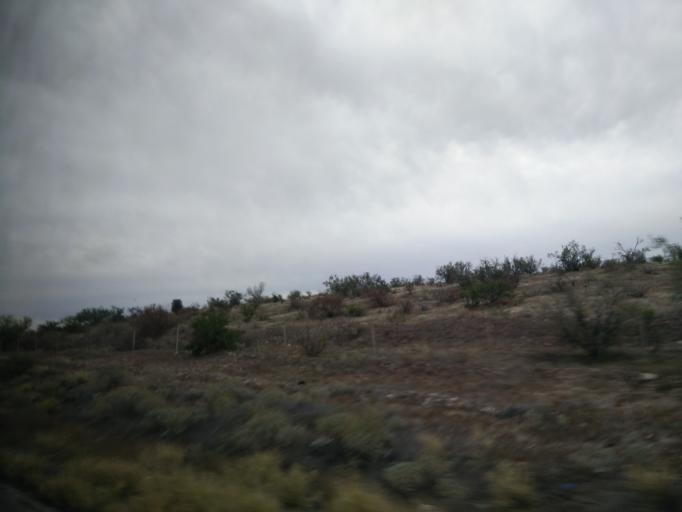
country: MX
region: Sonora
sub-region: Hermosillo
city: Miguel Aleman (La Doce)
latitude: 28.5042
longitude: -111.0455
